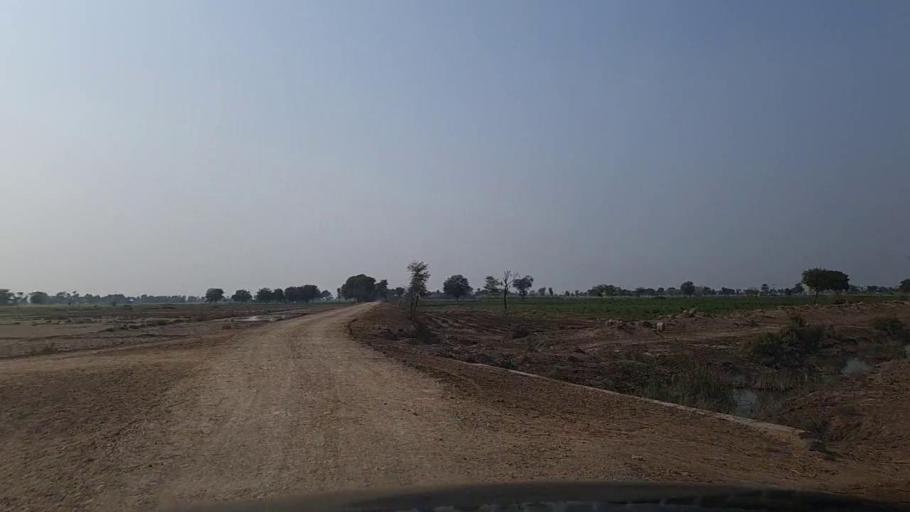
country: PK
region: Sindh
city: Daur
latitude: 26.3860
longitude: 68.4029
